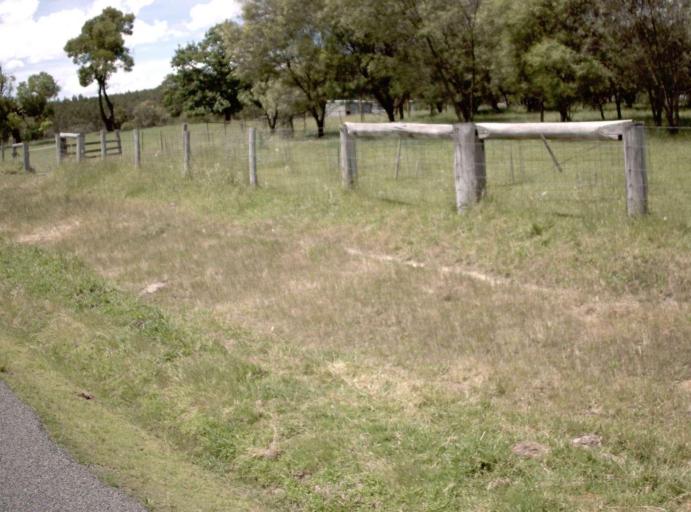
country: AU
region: New South Wales
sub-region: Bombala
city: Bombala
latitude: -37.4099
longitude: 149.0095
